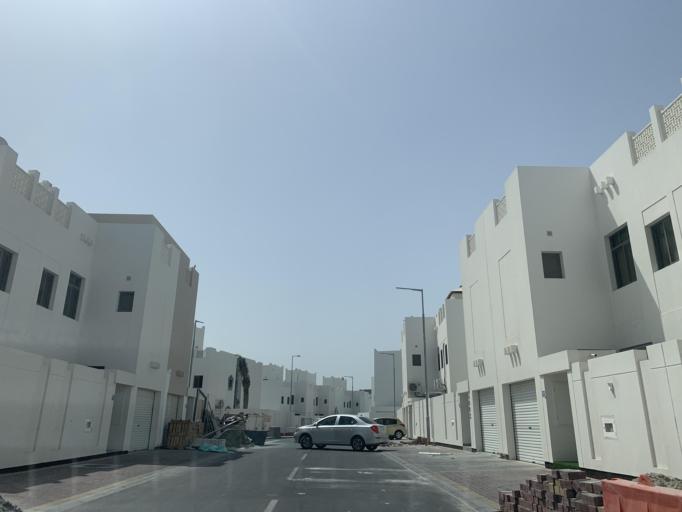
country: BH
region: Northern
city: Ar Rifa'
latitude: 26.1488
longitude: 50.5654
